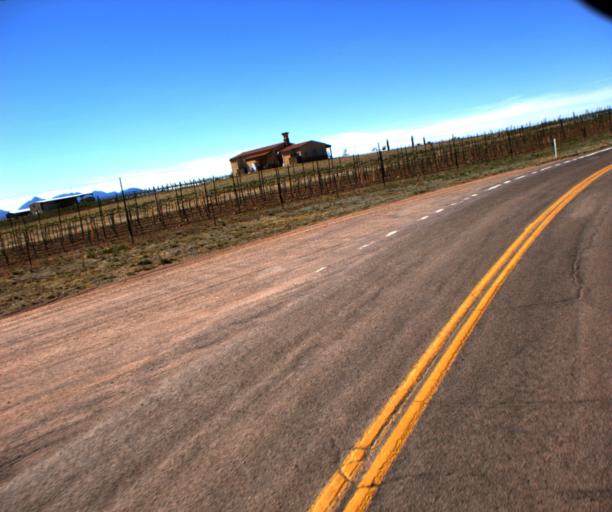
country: US
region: Arizona
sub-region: Cochise County
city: Huachuca City
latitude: 31.6086
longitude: -110.5870
